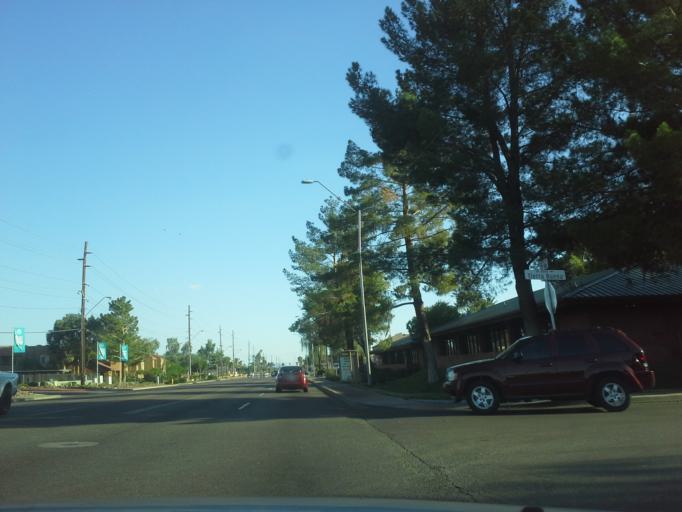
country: US
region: Arizona
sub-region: Maricopa County
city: Glendale
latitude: 33.6290
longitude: -112.1338
